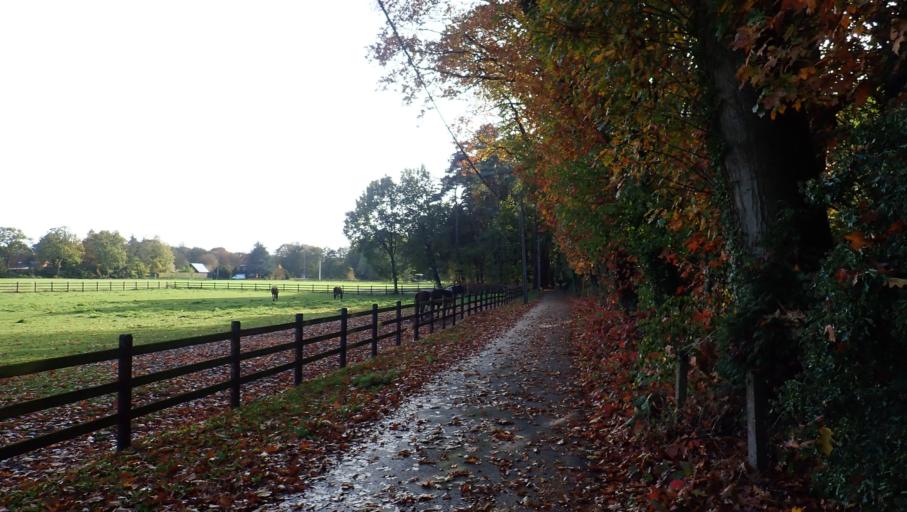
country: BE
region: Flanders
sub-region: Provincie Antwerpen
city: Zoersel
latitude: 51.2709
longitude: 4.6907
